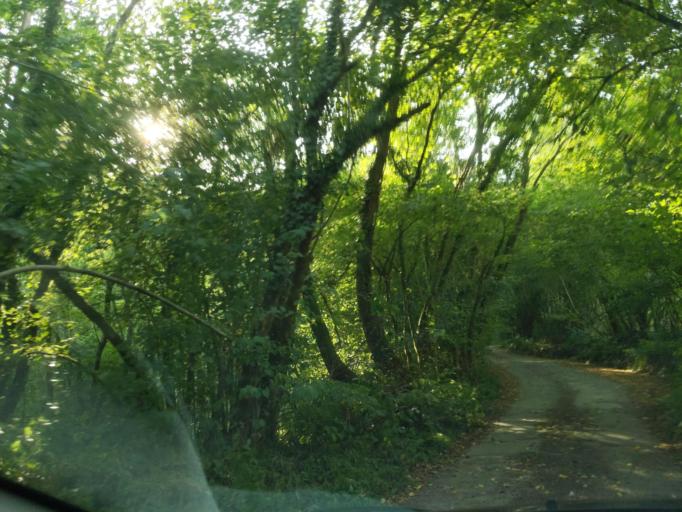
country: GB
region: England
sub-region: Devon
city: Winkleigh
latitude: 50.9668
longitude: -3.9665
